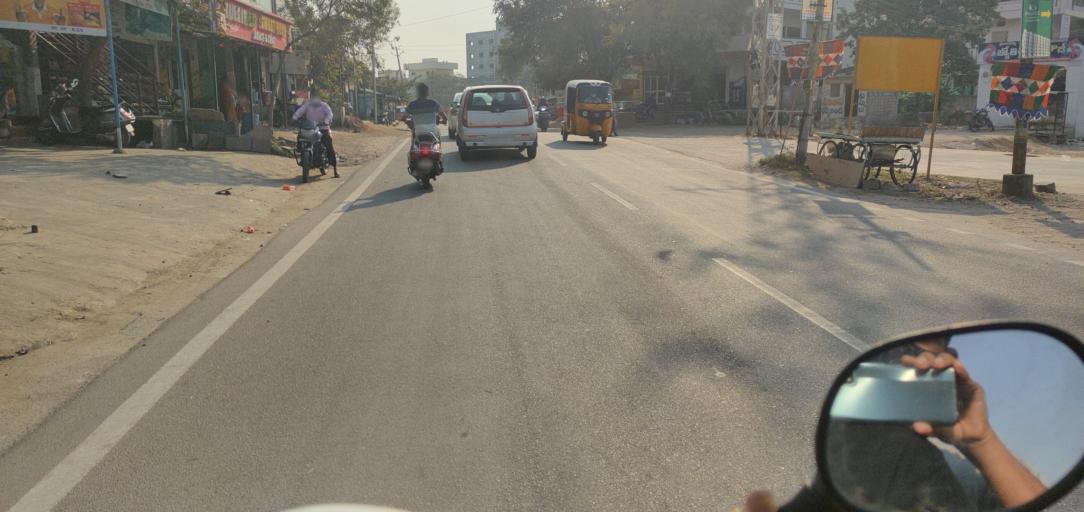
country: IN
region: Telangana
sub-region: Rangareddi
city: Lal Bahadur Nagar
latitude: 17.3337
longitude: 78.6122
